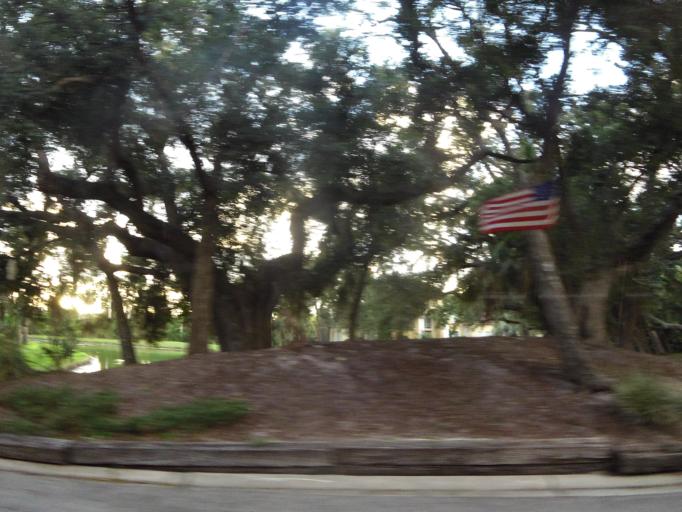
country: US
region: Florida
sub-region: Saint Johns County
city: Palm Valley
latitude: 30.1574
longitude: -81.3579
